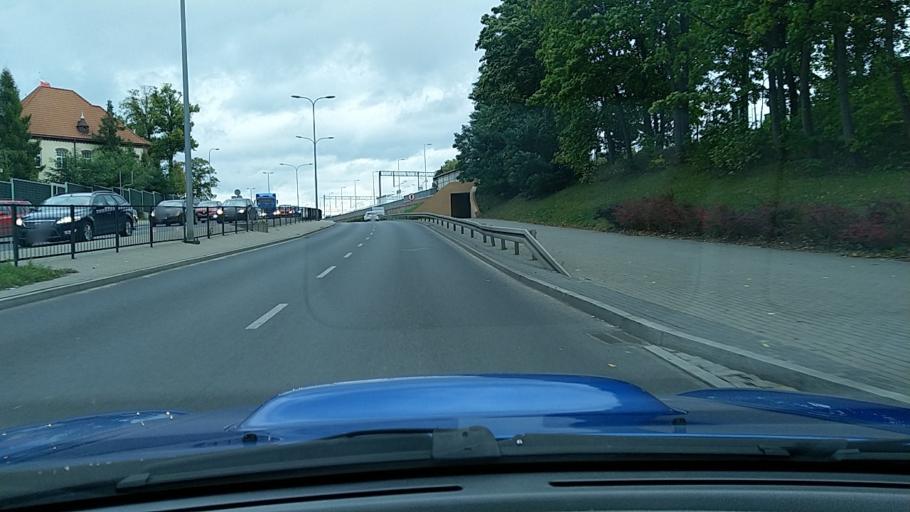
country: PL
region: Warmian-Masurian Voivodeship
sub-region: Olsztyn
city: Kortowo
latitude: 53.7781
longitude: 20.4656
